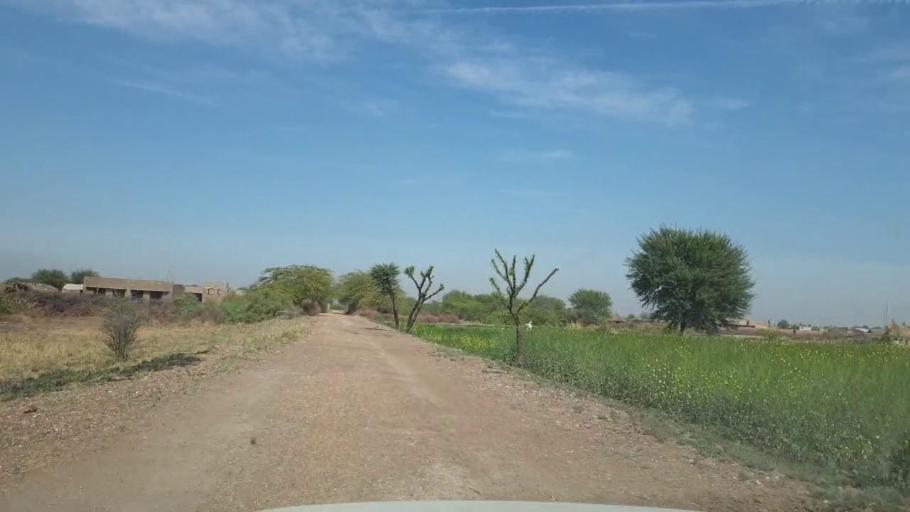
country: PK
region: Sindh
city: Mirpur Khas
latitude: 25.6243
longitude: 69.1960
